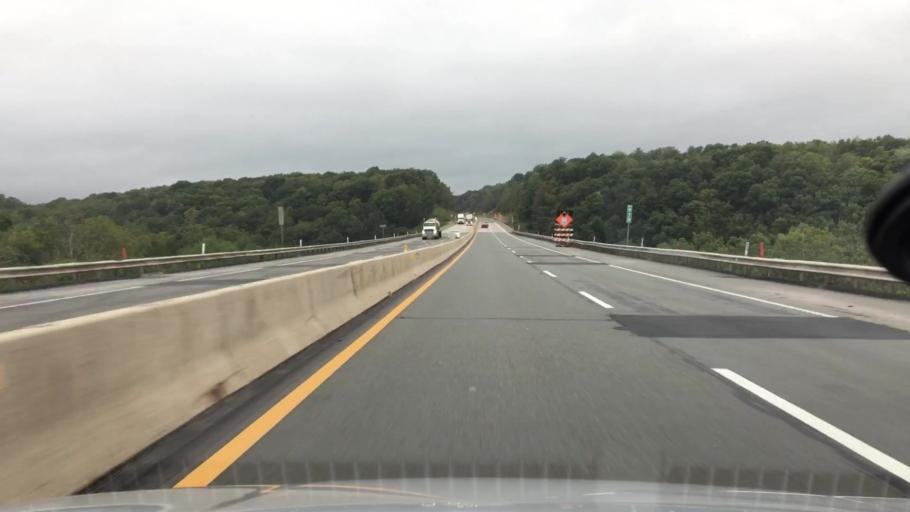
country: US
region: Pennsylvania
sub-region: Luzerne County
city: White Haven
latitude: 41.1020
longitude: -75.7477
